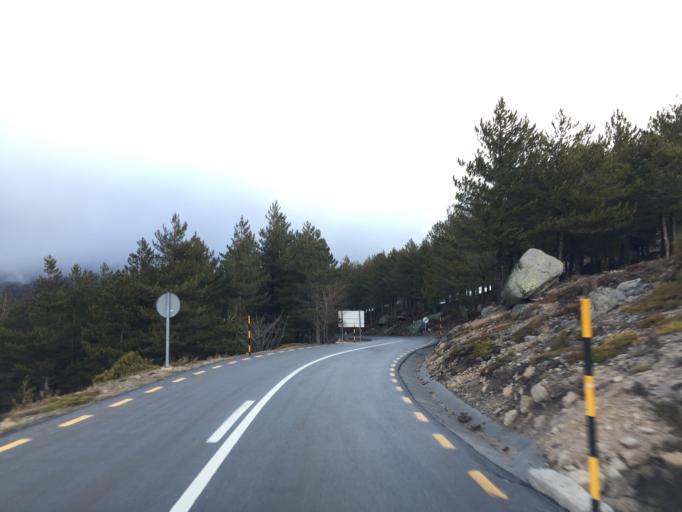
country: PT
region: Castelo Branco
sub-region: Covilha
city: Covilha
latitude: 40.3190
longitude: -7.5743
